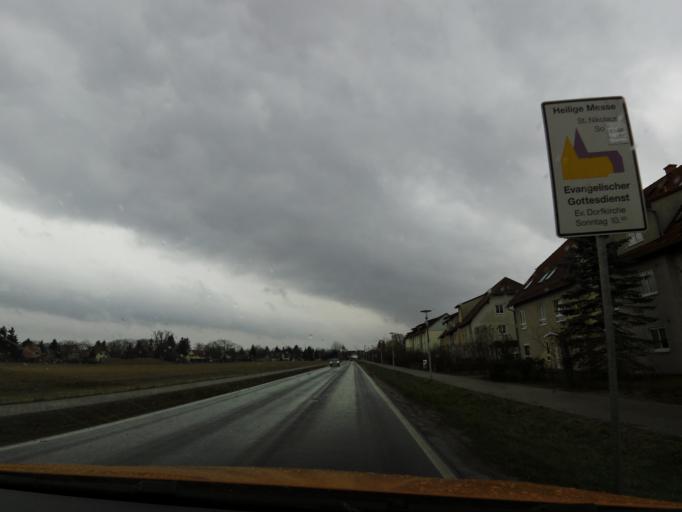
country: DE
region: Brandenburg
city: Rangsdorf
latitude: 52.3402
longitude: 13.3994
